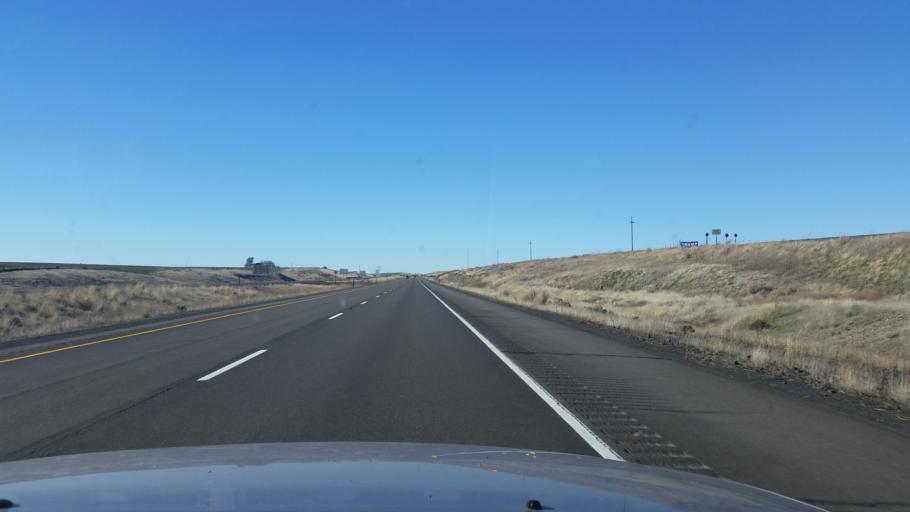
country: US
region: Washington
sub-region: Adams County
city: Ritzville
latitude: 47.1113
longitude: -118.4178
